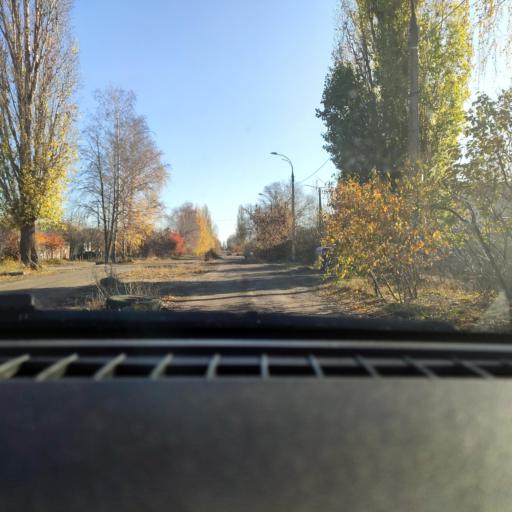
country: RU
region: Voronezj
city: Maslovka
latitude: 51.6313
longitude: 39.2761
